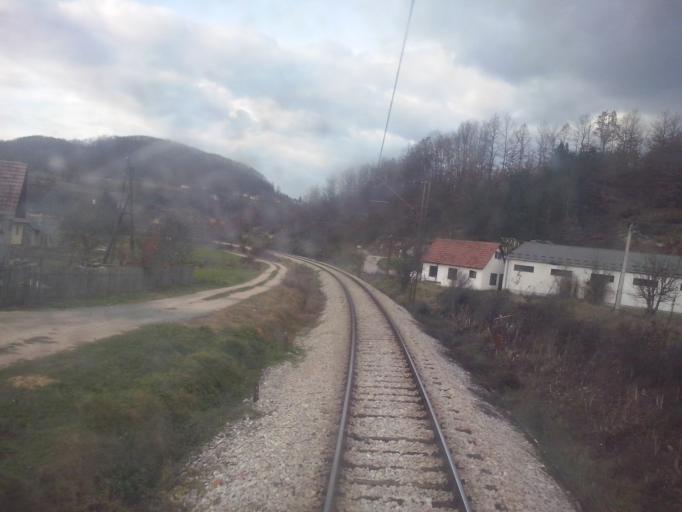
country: RS
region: Central Serbia
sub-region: Zlatiborski Okrug
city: Kosjeric
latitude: 43.9734
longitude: 19.9539
